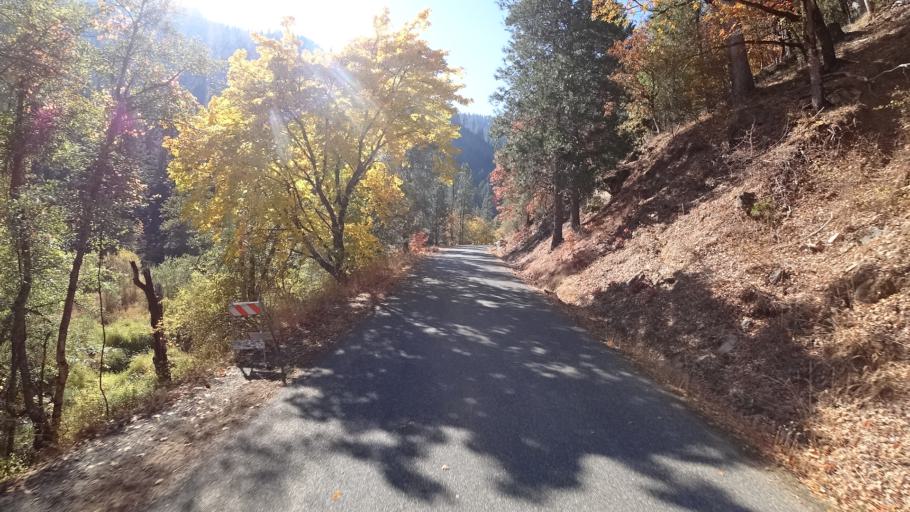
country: US
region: California
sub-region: Siskiyou County
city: Happy Camp
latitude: 41.6343
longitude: -123.0815
